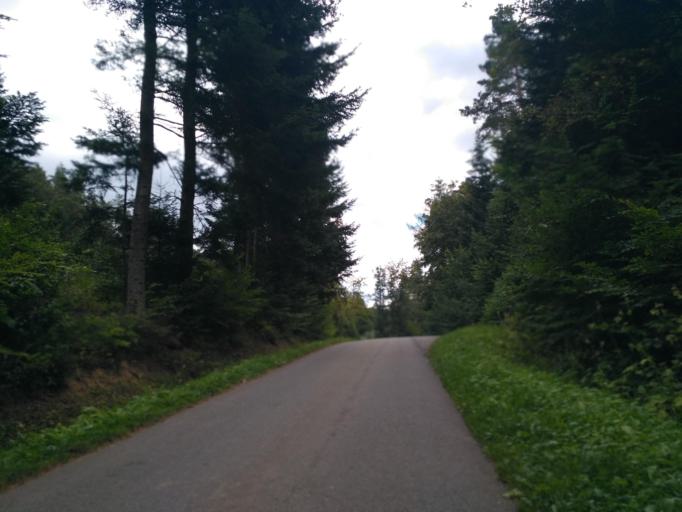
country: PL
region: Subcarpathian Voivodeship
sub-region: Powiat rzeszowski
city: Dynow
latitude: 49.7655
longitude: 22.2722
